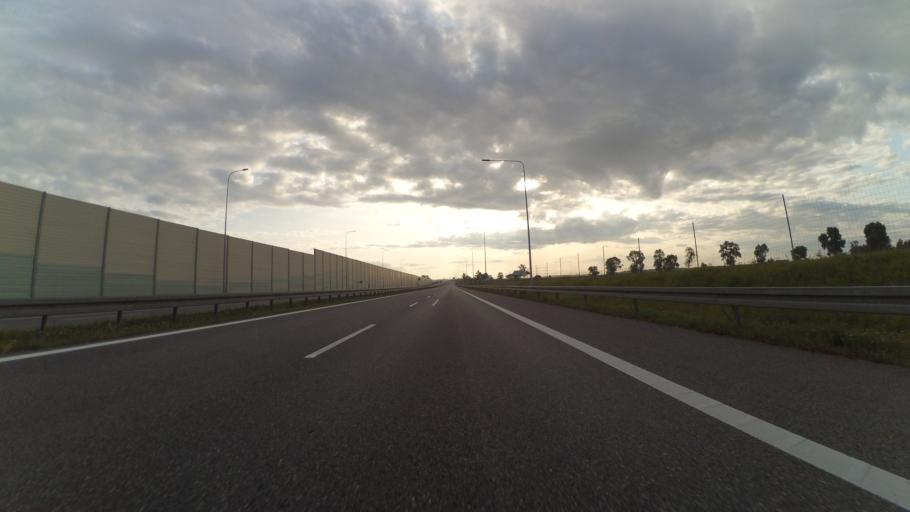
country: PL
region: Podlasie
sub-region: Powiat zambrowski
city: Zambrow
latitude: 53.0047
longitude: 22.2780
